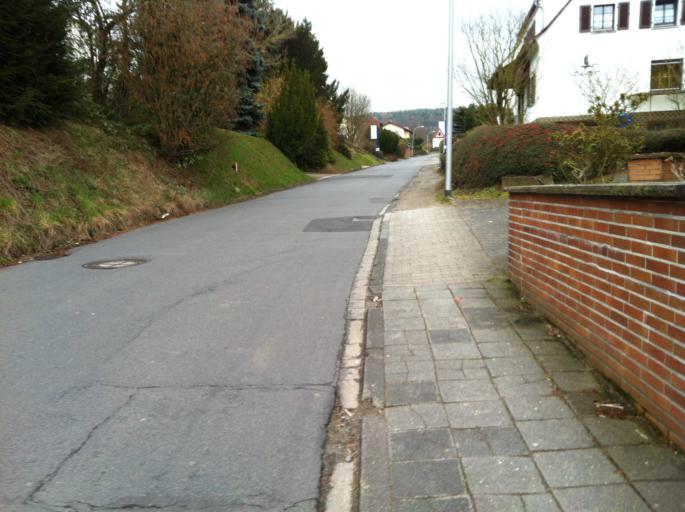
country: DE
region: Hesse
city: Michelstadt
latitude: 49.6754
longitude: 9.0105
